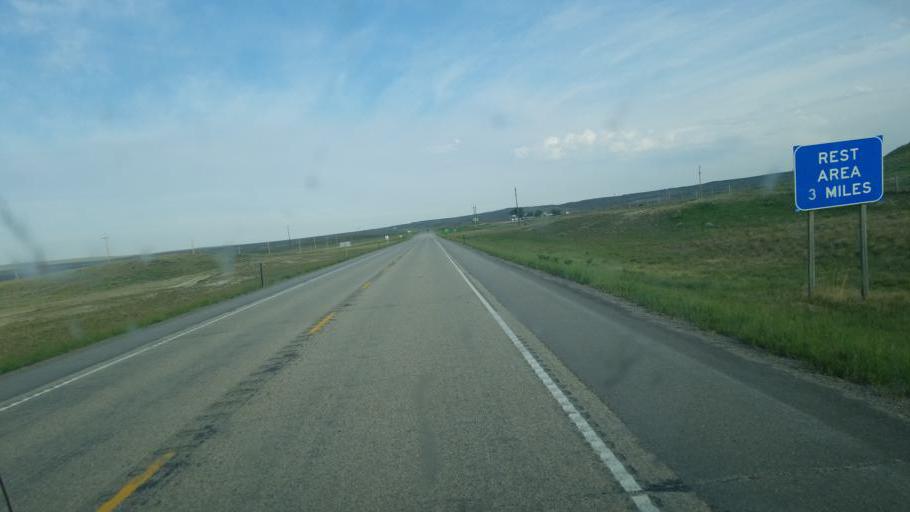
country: US
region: Wyoming
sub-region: Natrona County
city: Mills
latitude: 43.0697
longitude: -107.1903
